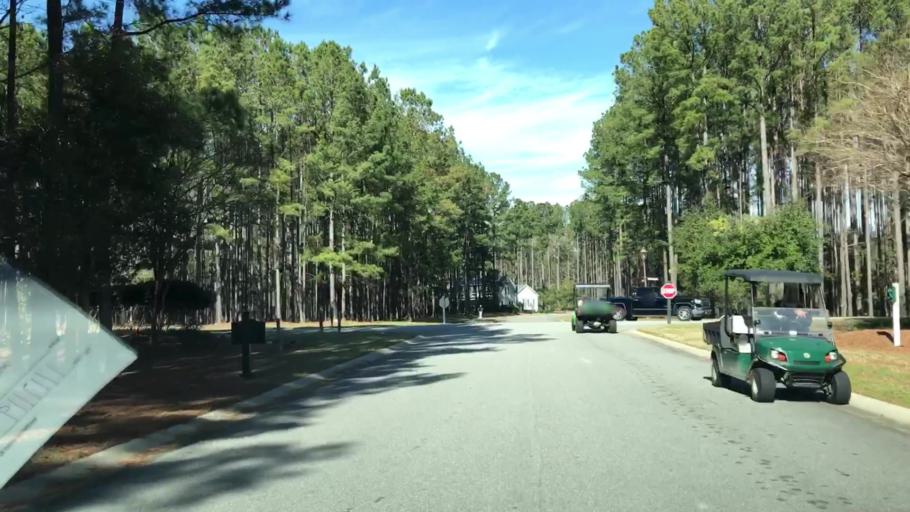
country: US
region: South Carolina
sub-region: Beaufort County
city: Bluffton
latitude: 32.2470
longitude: -80.9312
